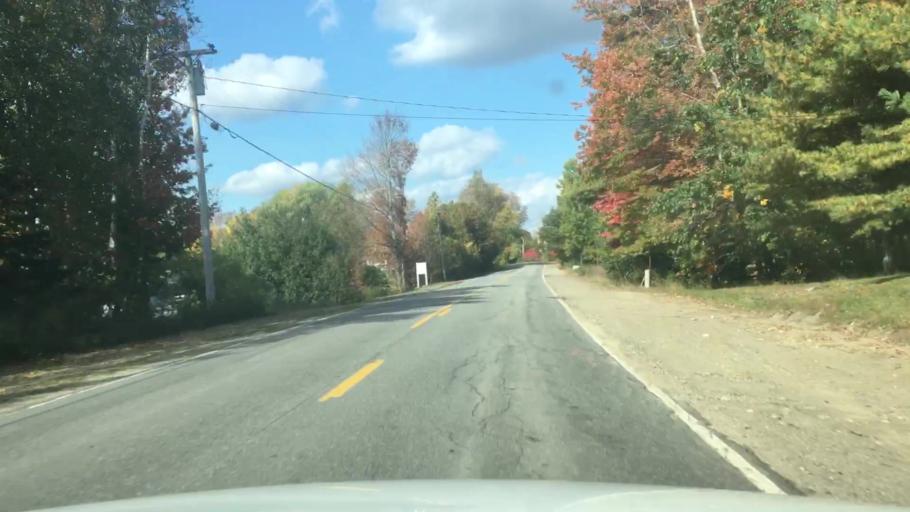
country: US
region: Maine
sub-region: Knox County
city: Union
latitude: 44.1834
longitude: -69.2601
